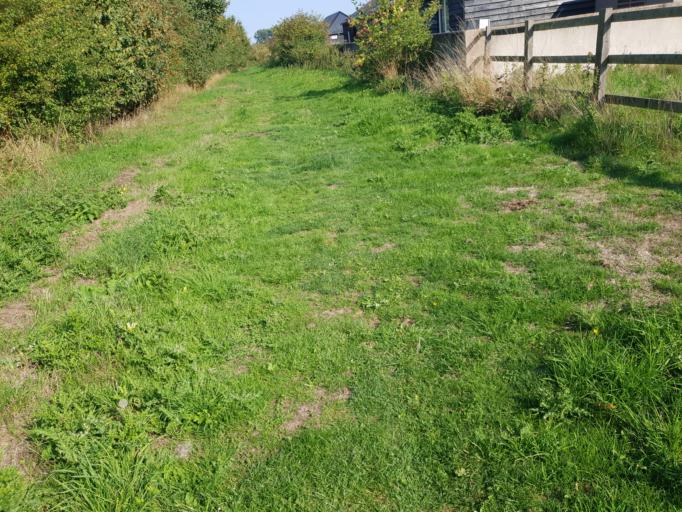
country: GB
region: England
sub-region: Suffolk
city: East Bergholt
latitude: 51.9527
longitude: 1.0141
